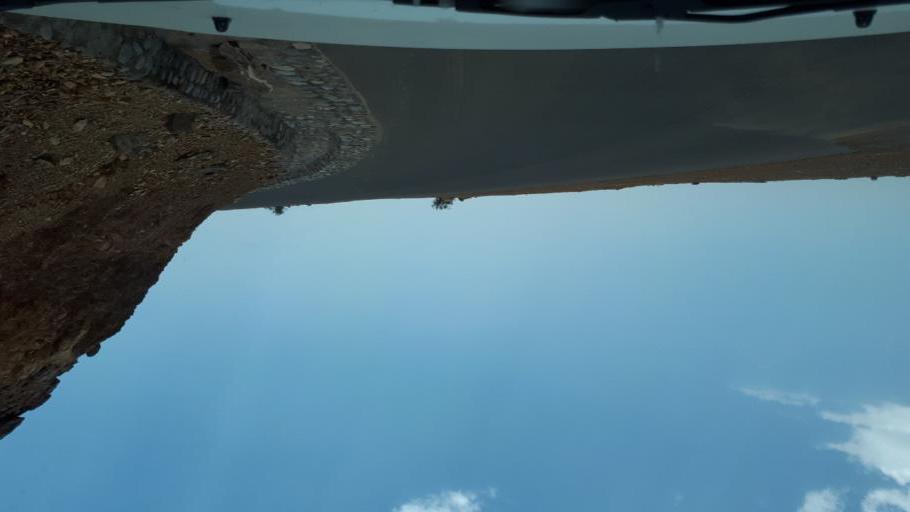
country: OM
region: Muhafazat ad Dakhiliyah
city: Bahla'
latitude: 23.2235
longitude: 57.2055
